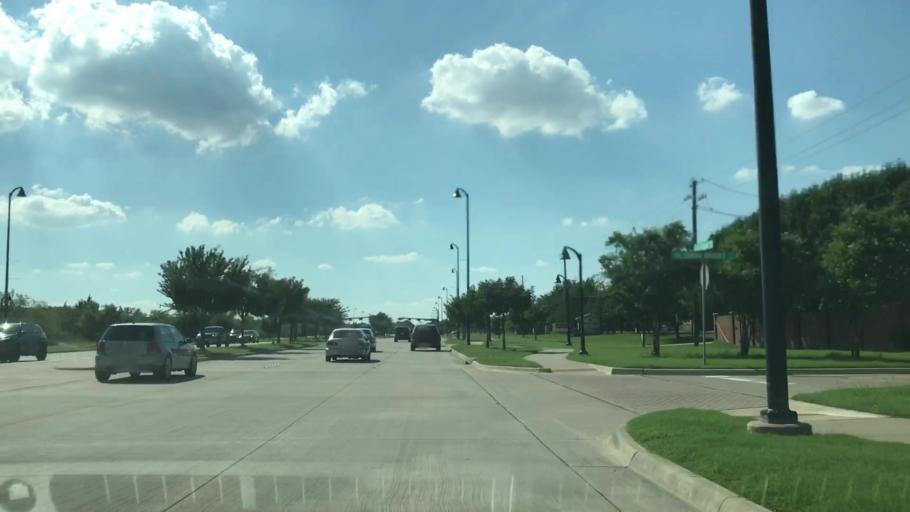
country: US
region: Texas
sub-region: Tarrant County
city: Keller
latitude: 32.9002
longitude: -97.2168
